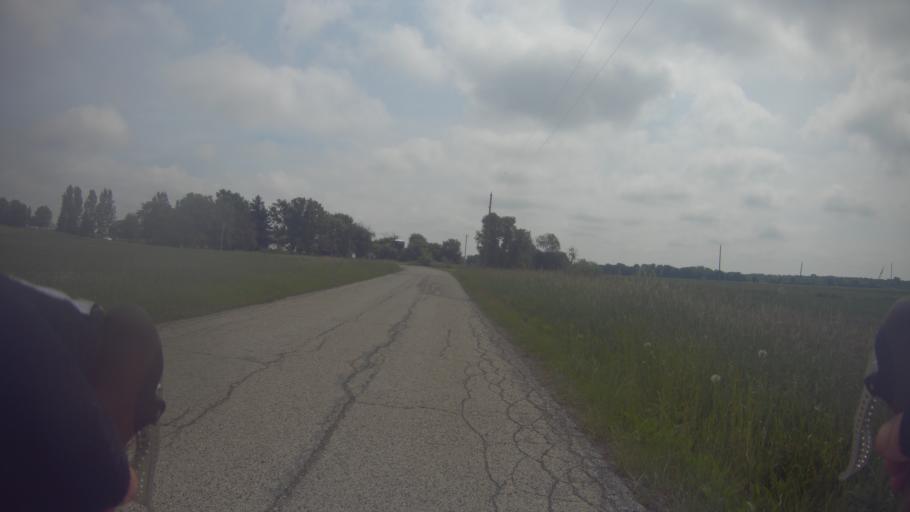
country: US
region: Wisconsin
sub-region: Jefferson County
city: Lake Ripley
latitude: 42.9332
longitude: -88.9901
